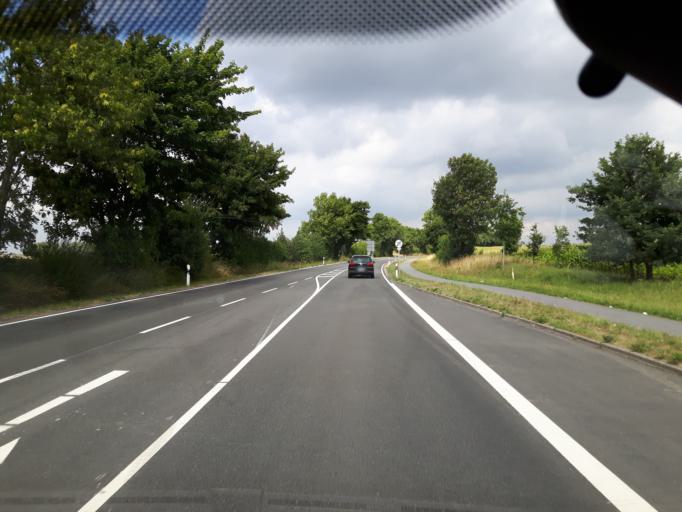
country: DE
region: Schleswig-Holstein
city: Holzbunge
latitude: 54.3832
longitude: 9.7111
